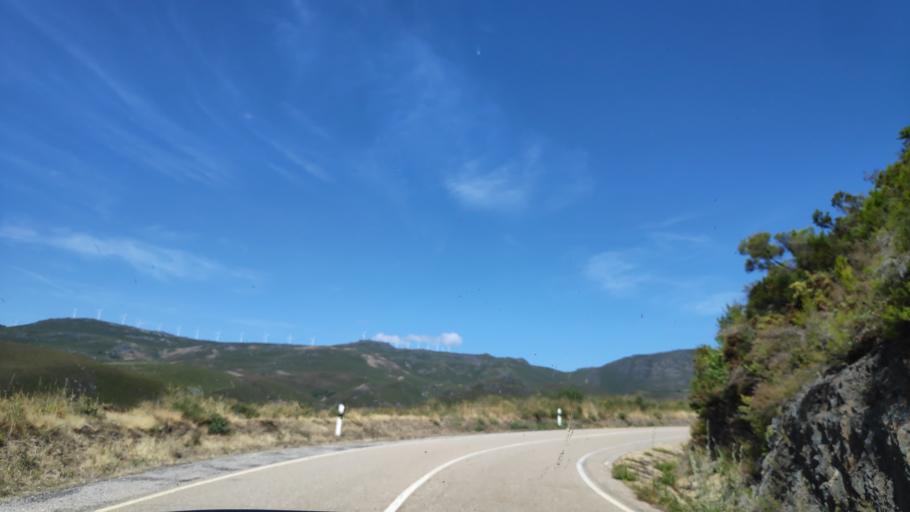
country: ES
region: Castille and Leon
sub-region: Provincia de Zamora
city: Requejo
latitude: 41.9744
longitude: -6.7129
